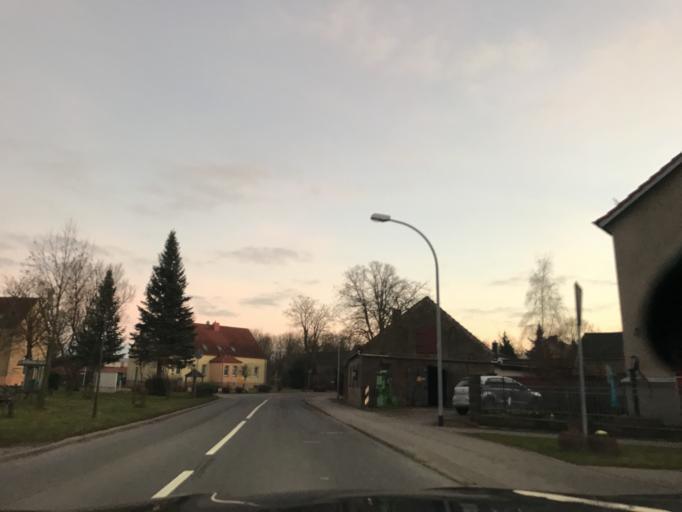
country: DE
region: Brandenburg
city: Ketzin
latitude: 52.5194
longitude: 12.8545
